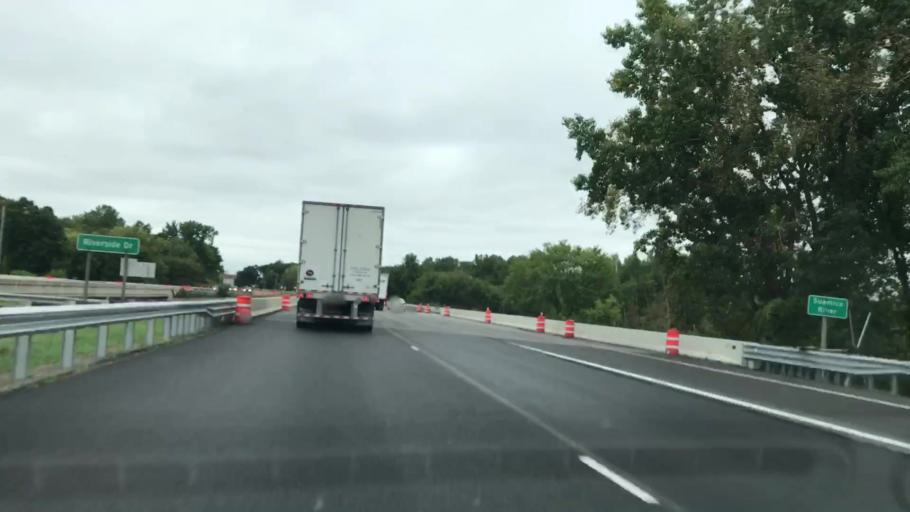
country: US
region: Wisconsin
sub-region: Brown County
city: Suamico
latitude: 44.6321
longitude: -88.0476
